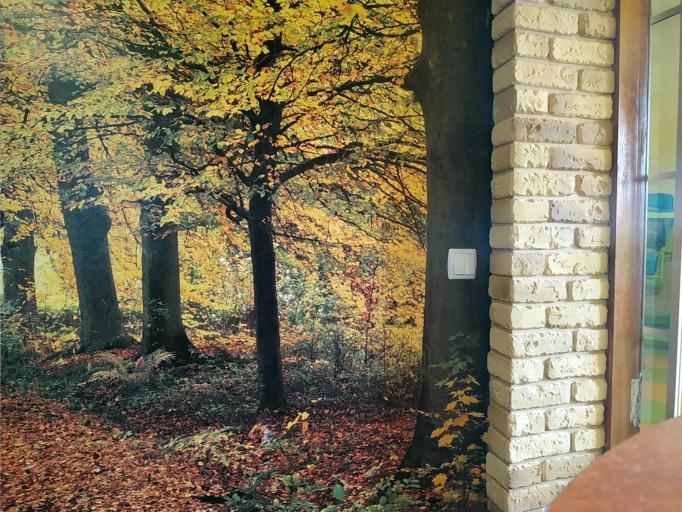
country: RU
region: Smolensk
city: Katyn'
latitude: 54.8865
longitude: 31.7994
